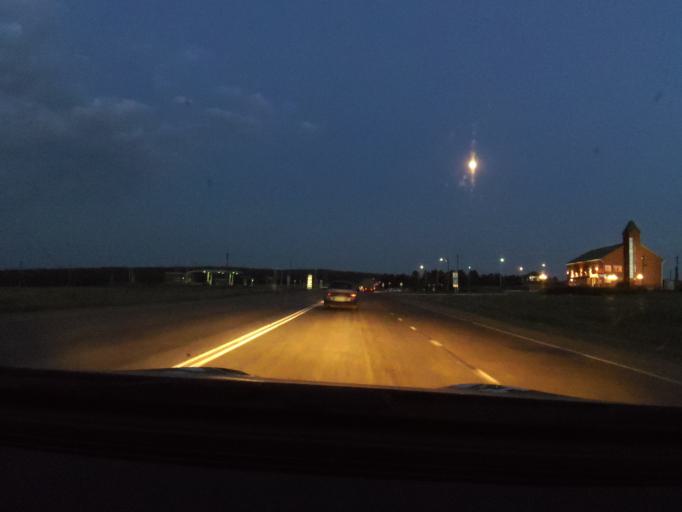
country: RU
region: Bashkortostan
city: Duvan
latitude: 55.9167
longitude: 58.2097
